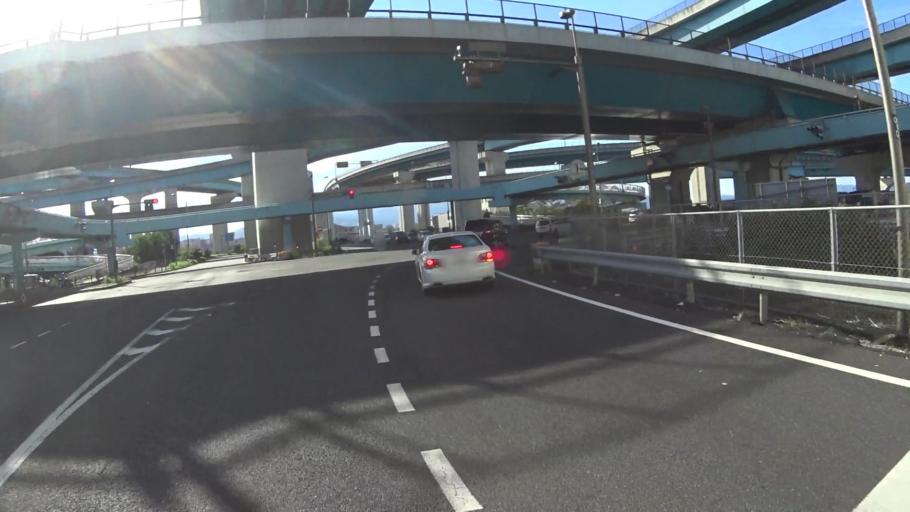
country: JP
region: Kyoto
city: Uji
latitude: 34.8959
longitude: 135.7501
